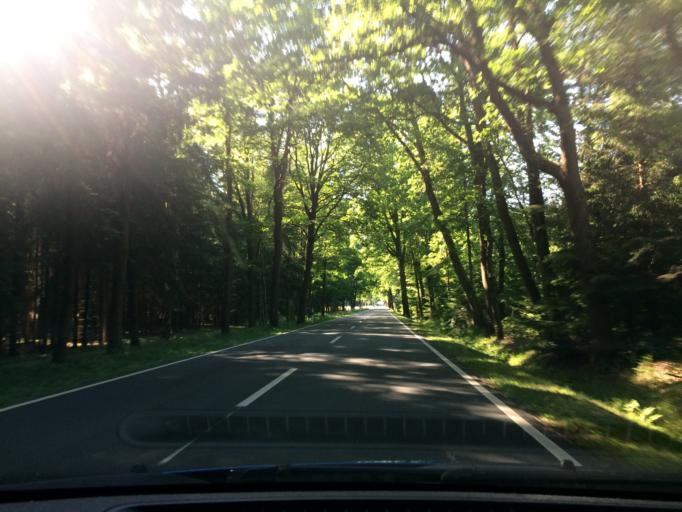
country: DE
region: Lower Saxony
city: Bad Fallingbostel
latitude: 52.9105
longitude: 9.7229
